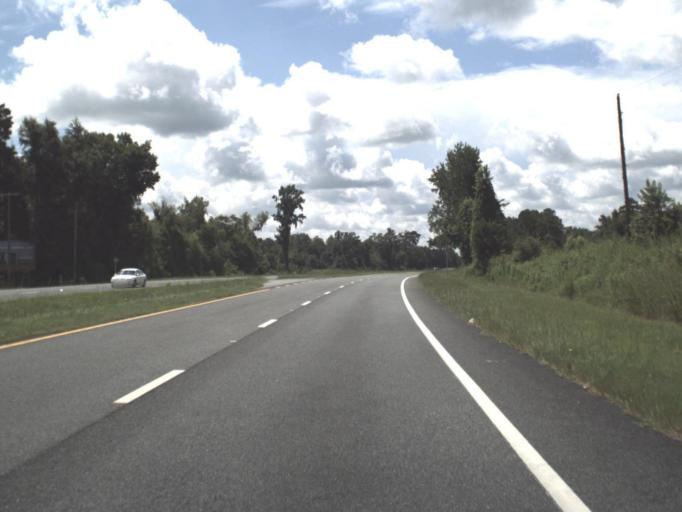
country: US
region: Florida
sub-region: Jefferson County
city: Monticello
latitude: 30.3664
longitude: -83.8036
